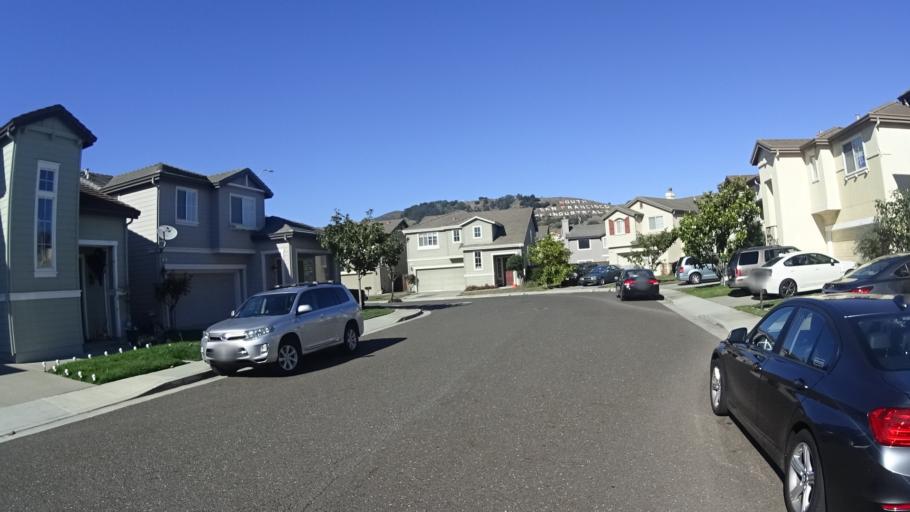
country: US
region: California
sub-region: San Mateo County
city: South San Francisco
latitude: 37.6537
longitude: -122.4212
